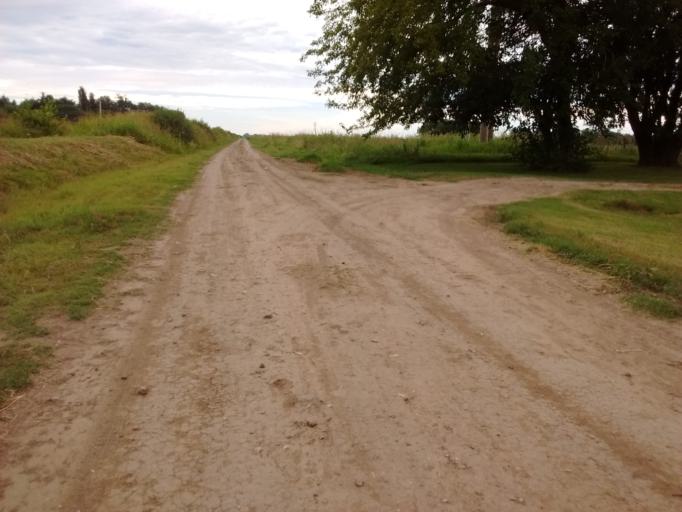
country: AR
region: Santa Fe
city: Funes
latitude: -32.9141
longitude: -60.8255
